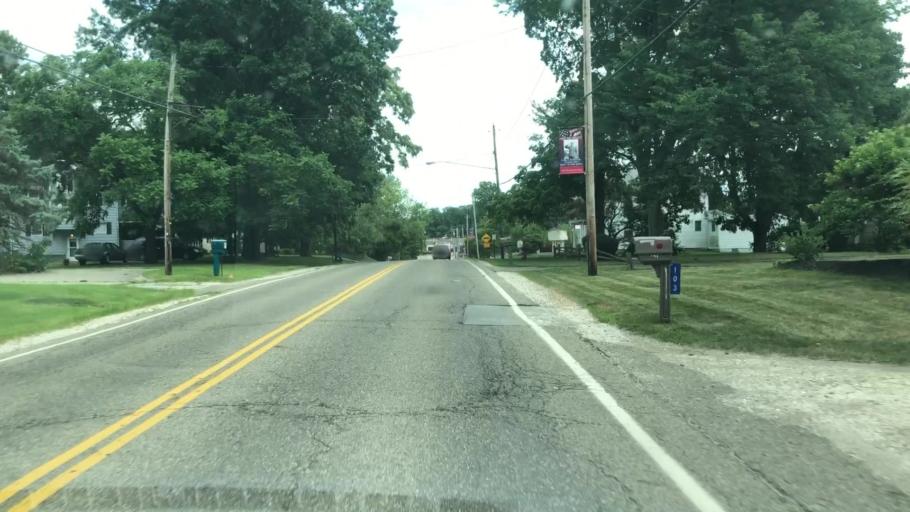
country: US
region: Ohio
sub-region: Summit County
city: Munroe Falls
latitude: 41.1397
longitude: -81.4431
